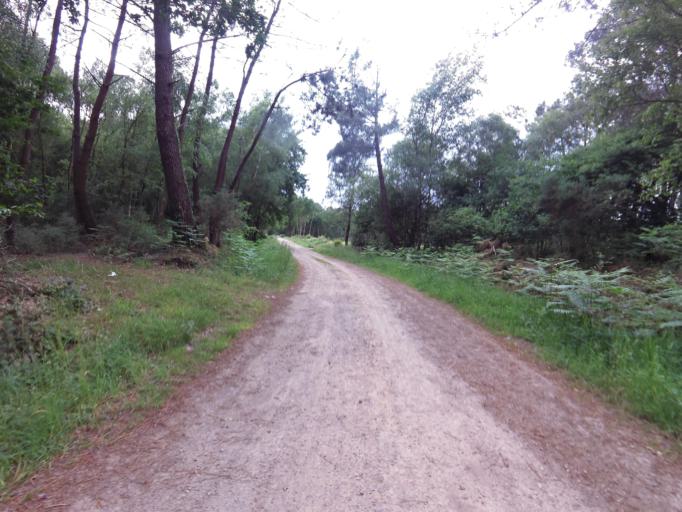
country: FR
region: Brittany
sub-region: Departement du Morbihan
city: Molac
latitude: 47.7378
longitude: -2.4279
